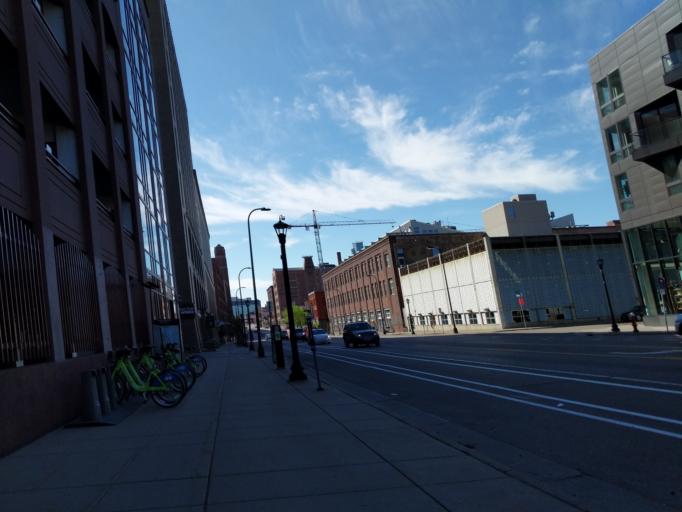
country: US
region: Minnesota
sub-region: Hennepin County
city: Minneapolis
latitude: 44.9901
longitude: -93.2800
